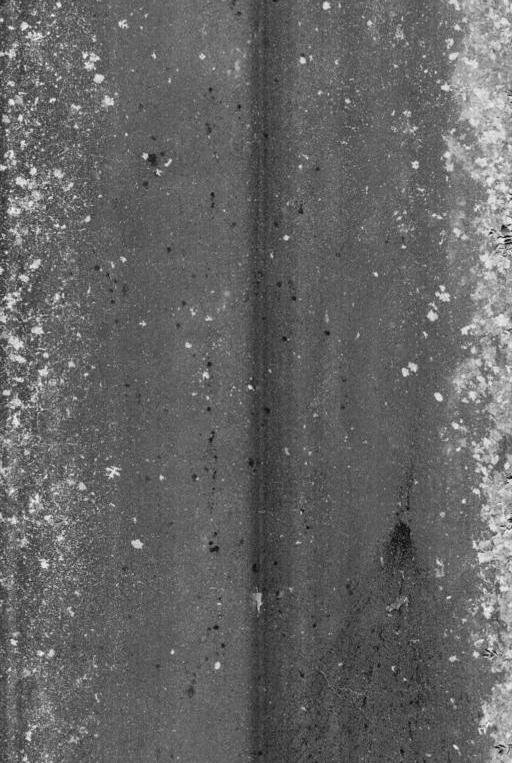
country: US
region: Maryland
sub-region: Montgomery County
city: Chevy Chase Village
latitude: 38.9367
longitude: -77.0537
